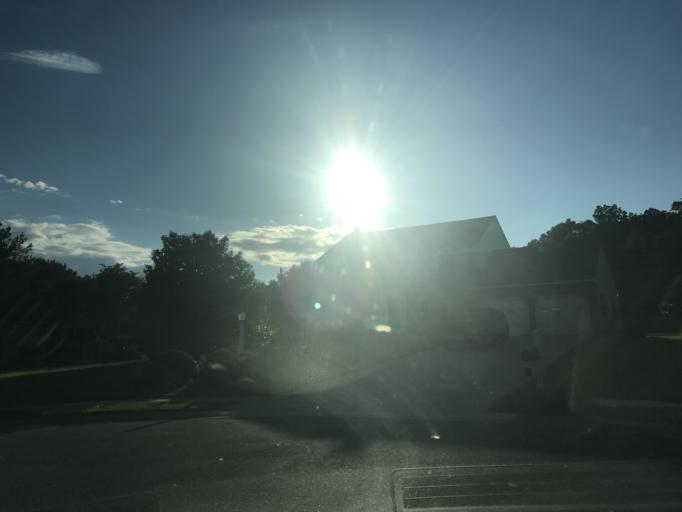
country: US
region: Maryland
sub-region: Harford County
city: South Bel Air
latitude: 39.5573
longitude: -76.3228
